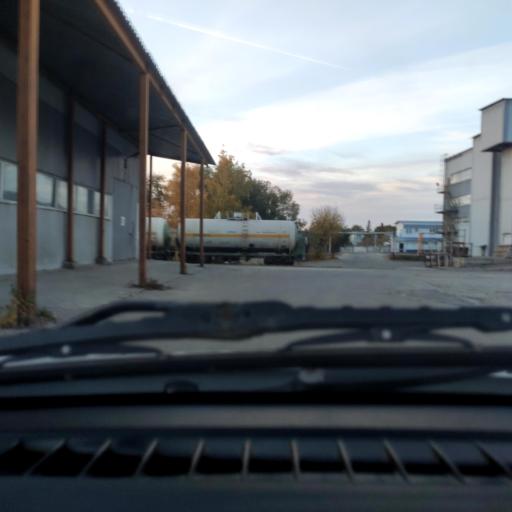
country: RU
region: Samara
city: Zhigulevsk
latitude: 53.4831
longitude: 49.4922
